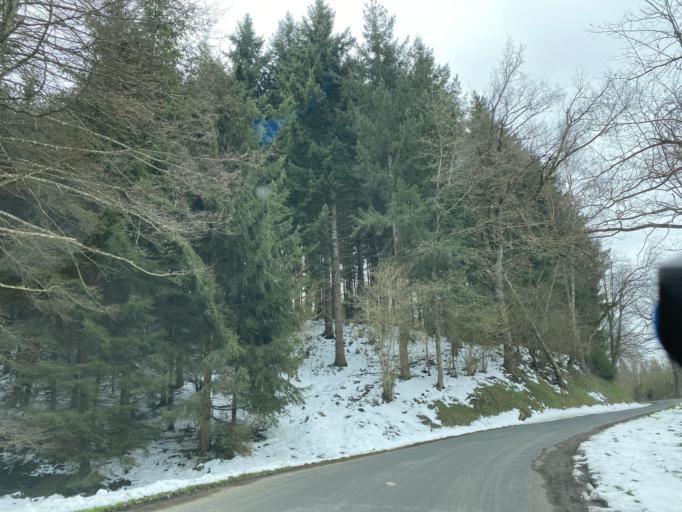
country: FR
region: Auvergne
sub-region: Departement du Puy-de-Dome
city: Escoutoux
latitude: 45.7941
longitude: 3.6179
